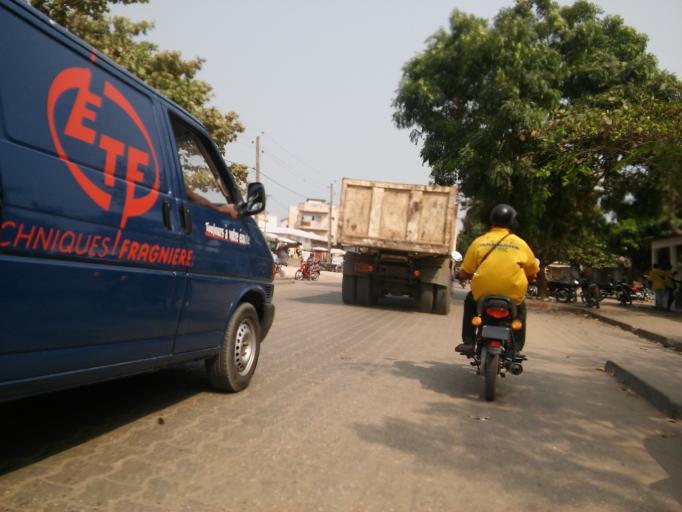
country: BJ
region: Littoral
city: Cotonou
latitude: 6.3907
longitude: 2.3980
